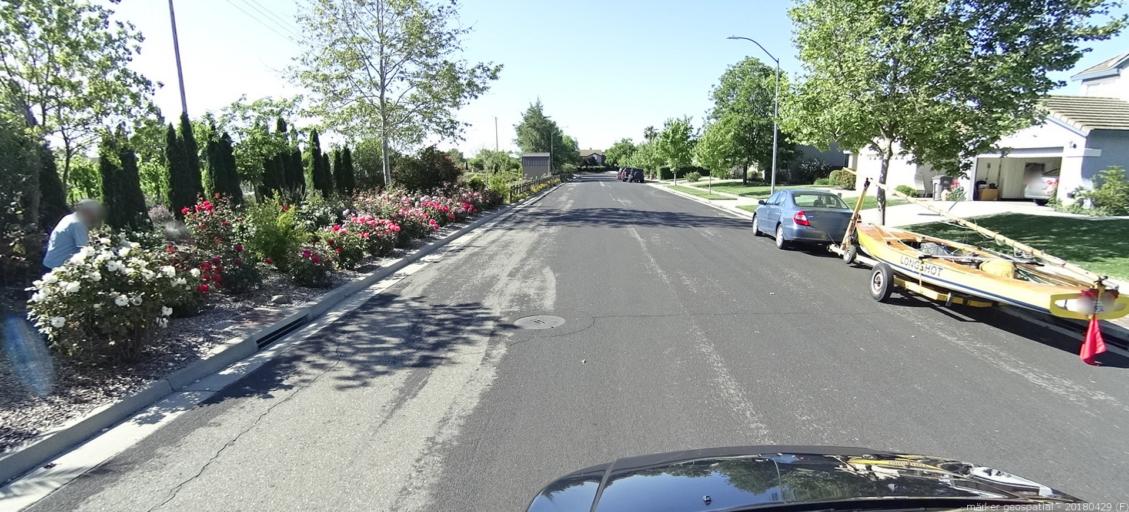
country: US
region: California
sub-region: Yolo County
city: West Sacramento
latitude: 38.5404
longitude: -121.5593
